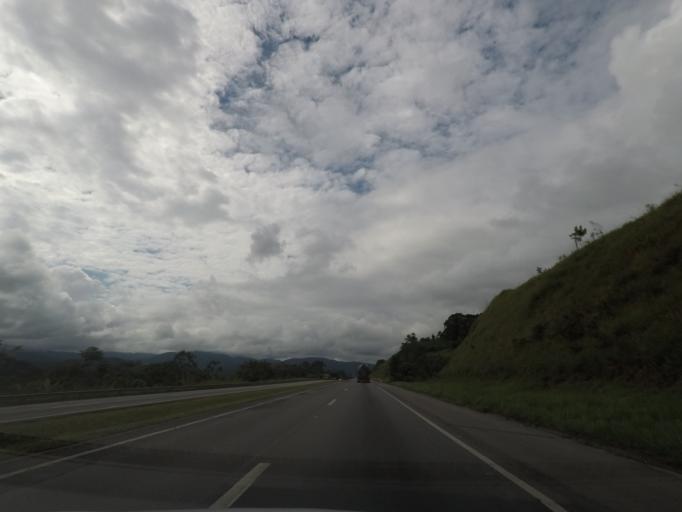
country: BR
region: Sao Paulo
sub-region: Miracatu
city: Miracatu
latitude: -24.1768
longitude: -47.3468
